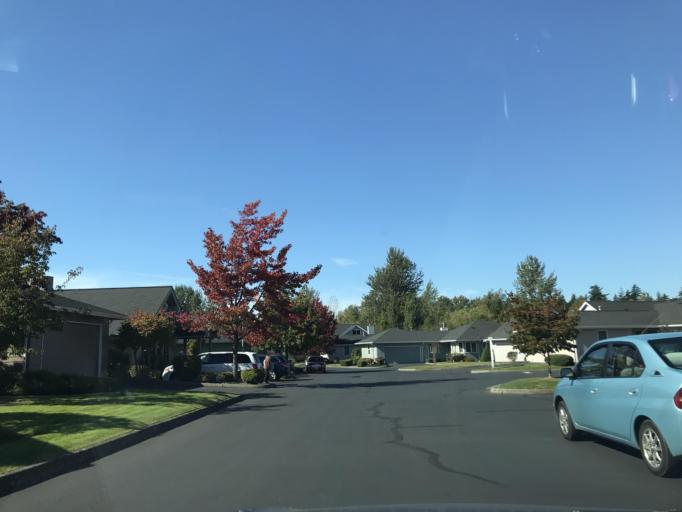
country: US
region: Washington
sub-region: Whatcom County
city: Bellingham
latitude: 48.7983
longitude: -122.5003
